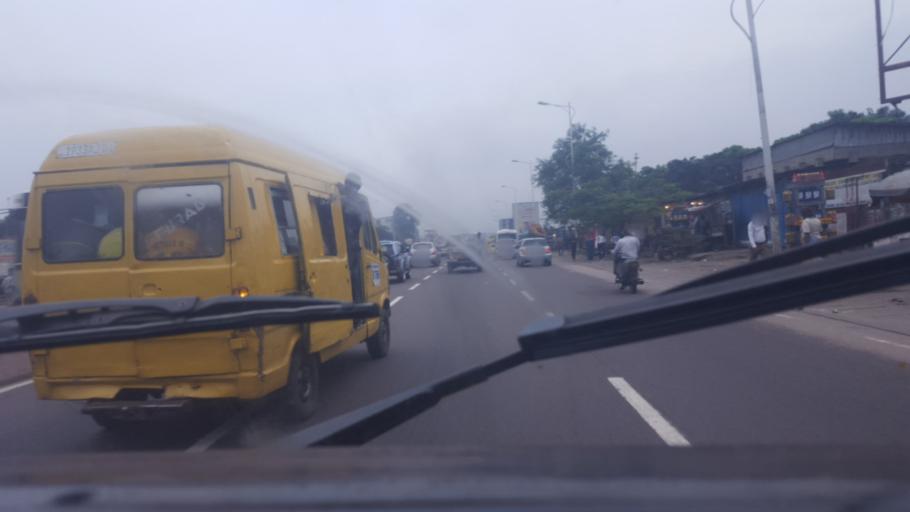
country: CD
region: Kinshasa
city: Kinshasa
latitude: -4.3362
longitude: 15.3257
